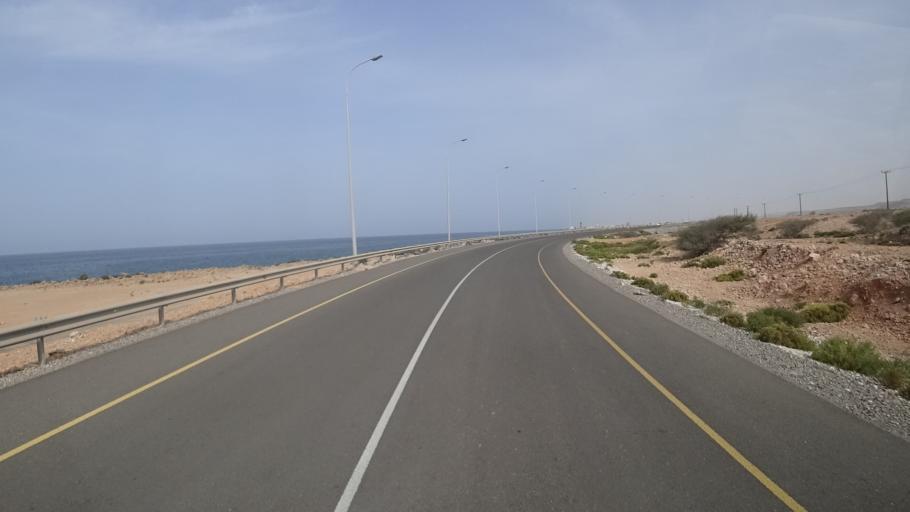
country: OM
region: Ash Sharqiyah
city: Sur
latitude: 23.0048
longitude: 59.1156
